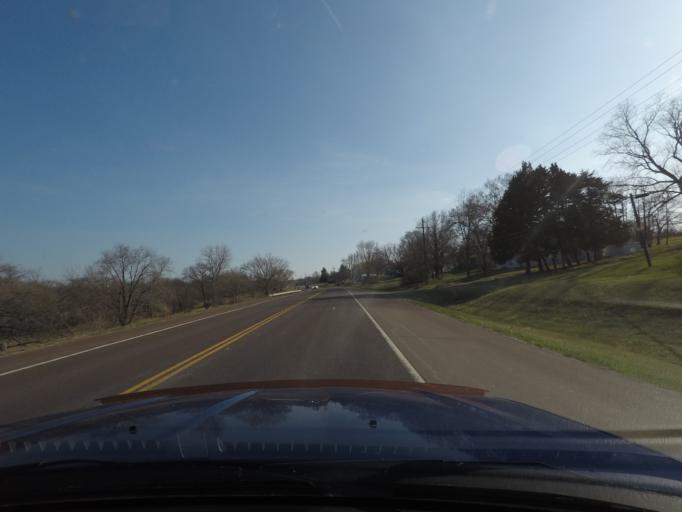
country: US
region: Kansas
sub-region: Douglas County
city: Lawrence
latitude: 39.0401
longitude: -95.3911
